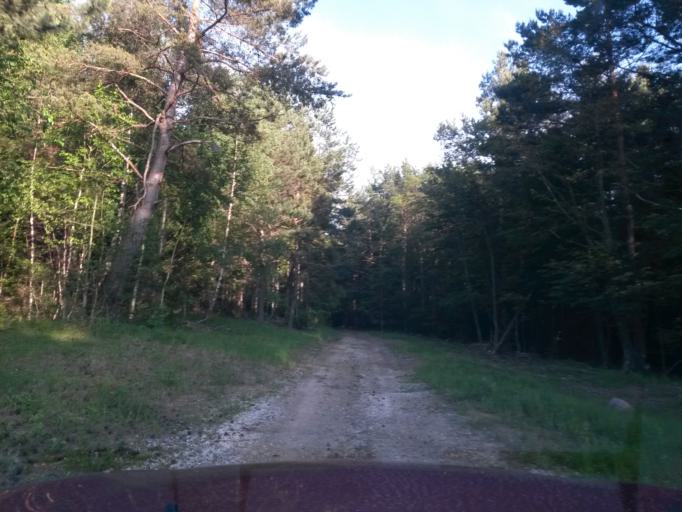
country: SK
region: Kosicky
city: Moldava nad Bodvou
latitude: 48.7426
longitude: 21.0286
